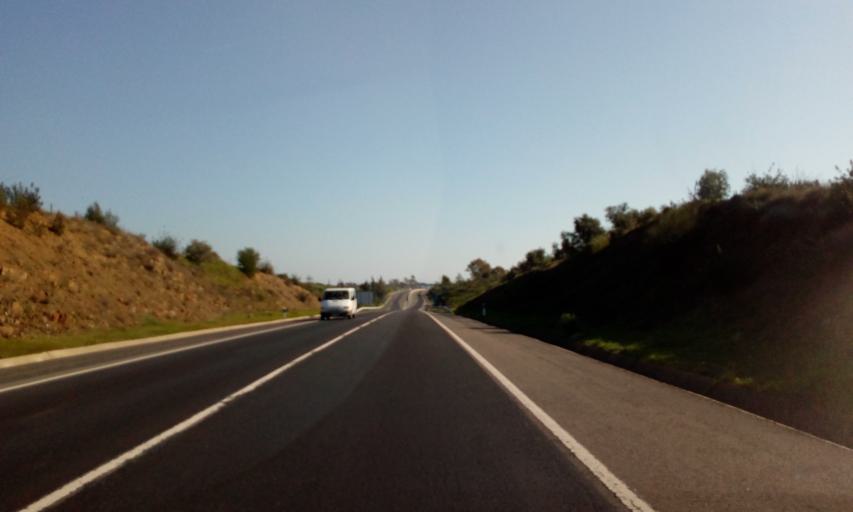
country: PT
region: Faro
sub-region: Castro Marim
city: Castro Marim
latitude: 37.2440
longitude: -7.4626
